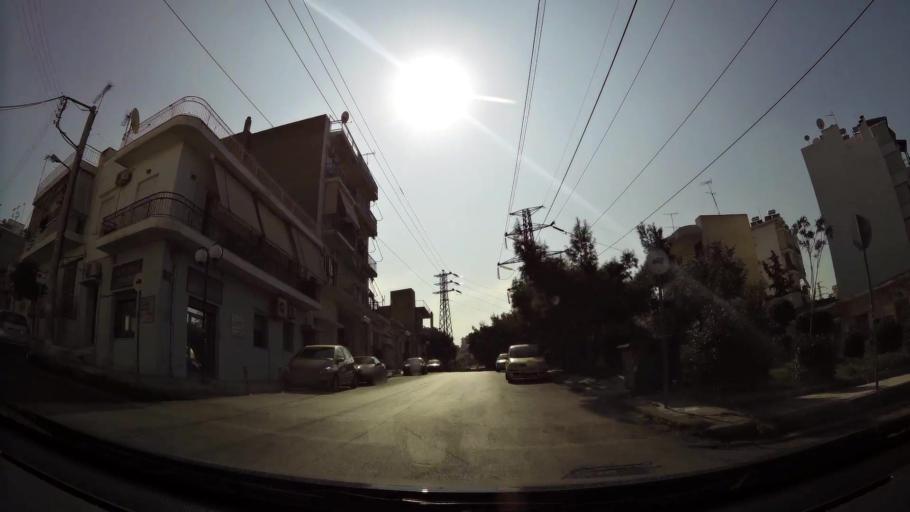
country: GR
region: Attica
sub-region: Nomos Piraios
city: Keratsini
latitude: 37.9566
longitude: 23.6156
